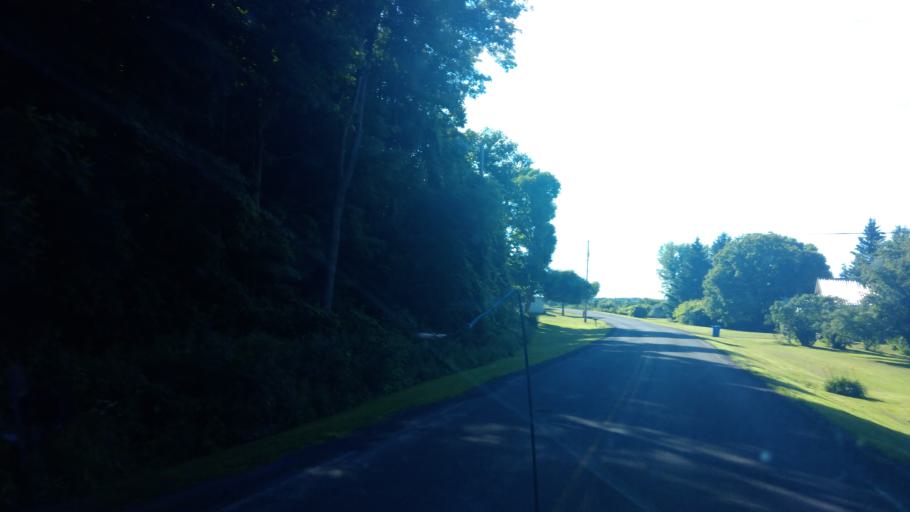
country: US
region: New York
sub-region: Wayne County
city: Lyons
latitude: 43.0109
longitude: -76.9781
